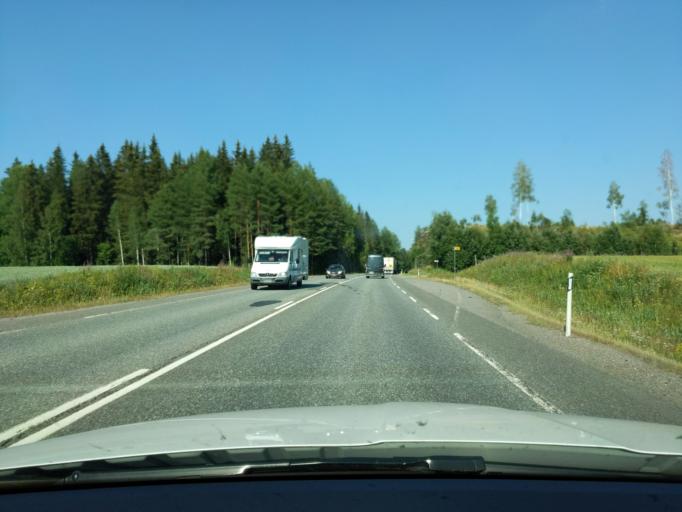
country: FI
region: Paijanne Tavastia
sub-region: Lahti
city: Hollola
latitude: 60.9617
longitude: 25.4492
